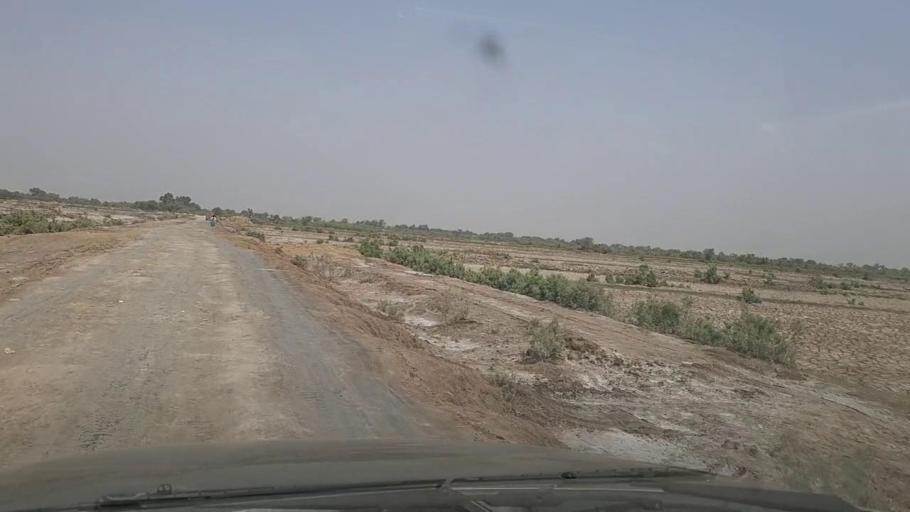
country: PK
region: Sindh
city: Thul
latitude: 28.3962
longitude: 68.7135
